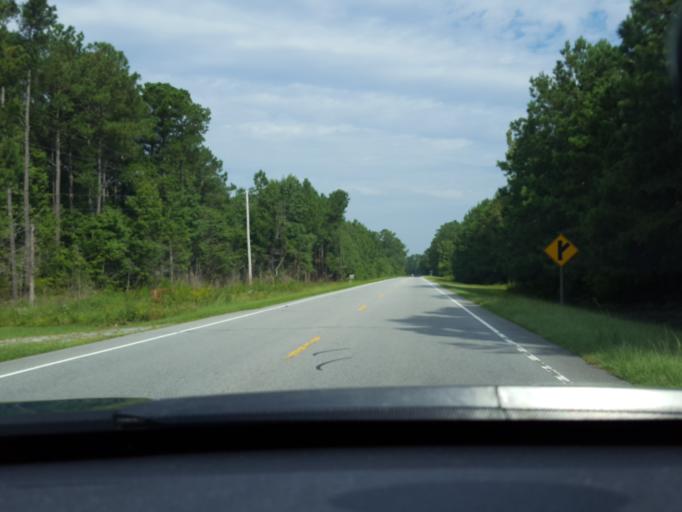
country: US
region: North Carolina
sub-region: Washington County
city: Plymouth
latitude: 35.9561
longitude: -76.7474
